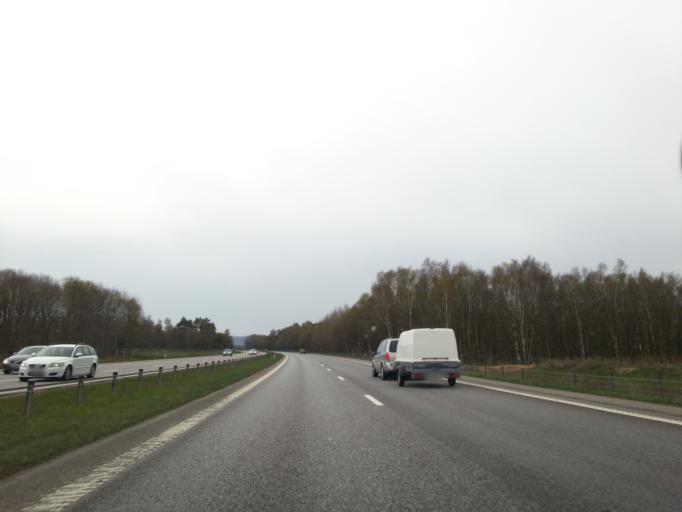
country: SE
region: Halland
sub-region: Laholms Kommun
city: Mellbystrand
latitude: 56.4710
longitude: 12.9419
